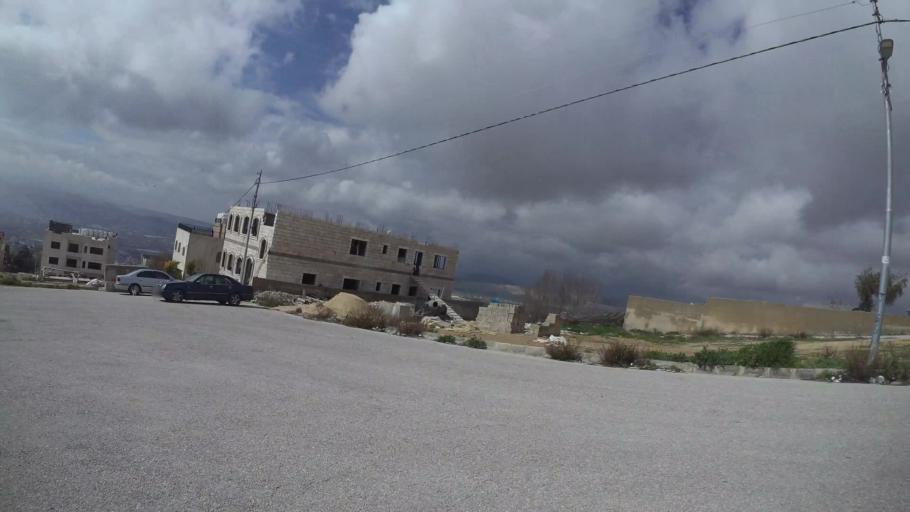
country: JO
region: Amman
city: Al Jubayhah
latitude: 32.0734
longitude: 35.8811
